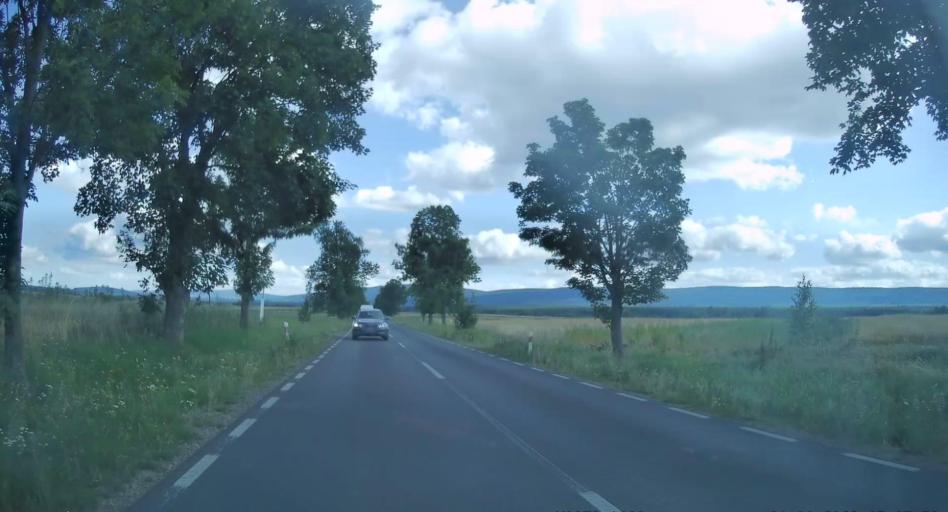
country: PL
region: Swietokrzyskie
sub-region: Powiat kielecki
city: Bodzentyn
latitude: 50.9286
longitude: 20.9812
